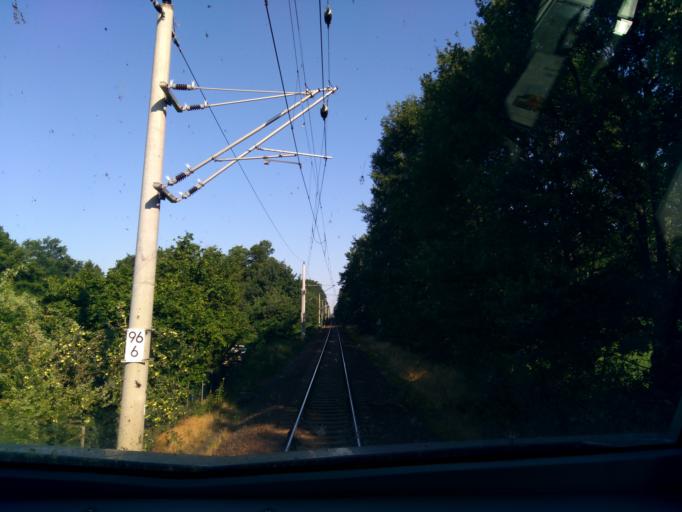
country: DE
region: Brandenburg
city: Vetschau
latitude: 51.7926
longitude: 14.0722
